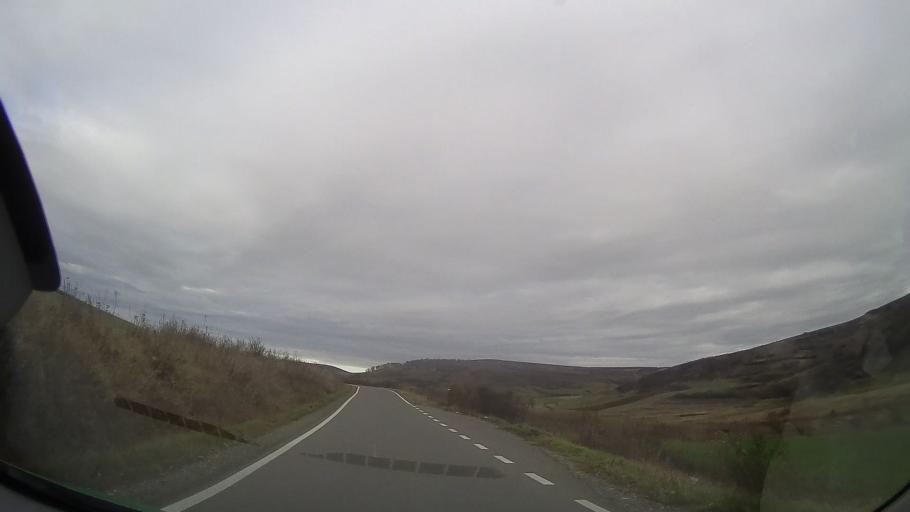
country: RO
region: Mures
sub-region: Comuna Faragau
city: Faragau
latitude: 46.7685
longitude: 24.5577
